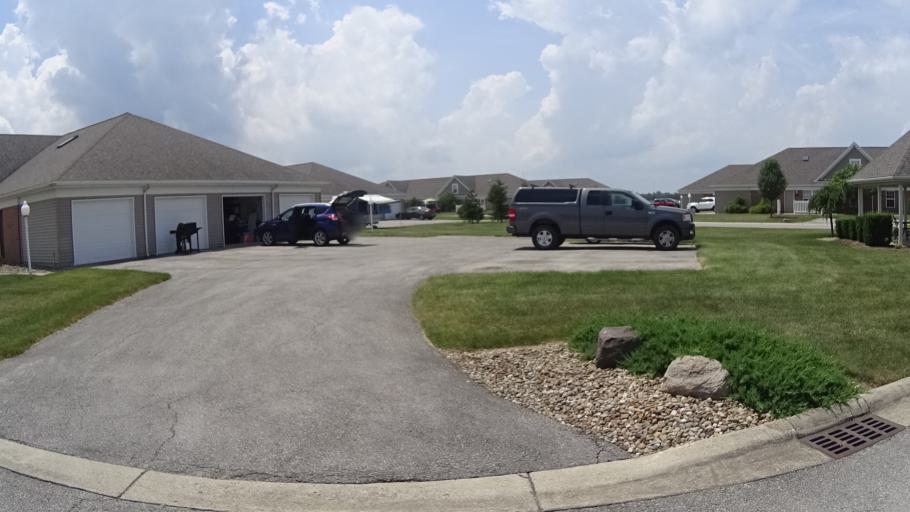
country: US
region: Ohio
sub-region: Lorain County
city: Vermilion
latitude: 41.4067
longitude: -82.3698
